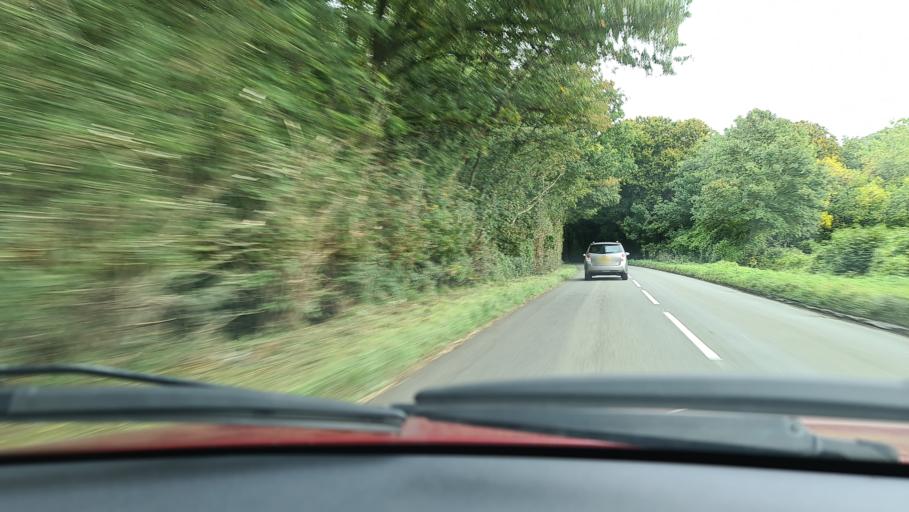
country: GB
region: England
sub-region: Oxfordshire
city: Somerton
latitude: 51.9245
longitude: -1.2414
